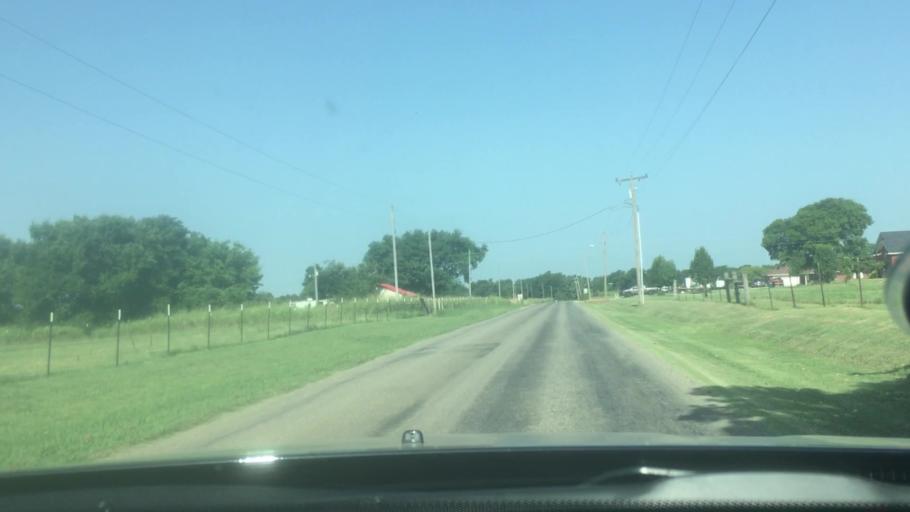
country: US
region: Oklahoma
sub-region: Bryan County
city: Calera
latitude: 33.9397
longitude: -96.4412
